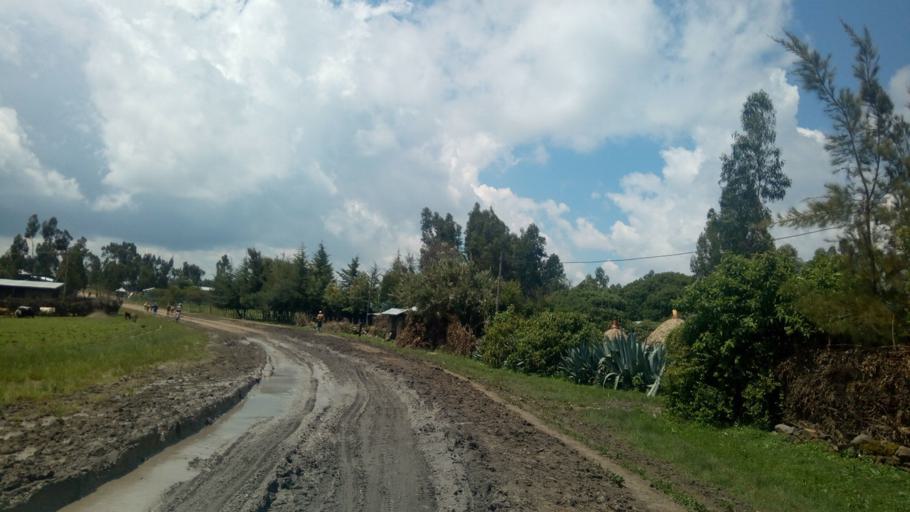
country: ET
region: Oromiya
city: Sendafa
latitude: 8.9980
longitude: 39.1274
